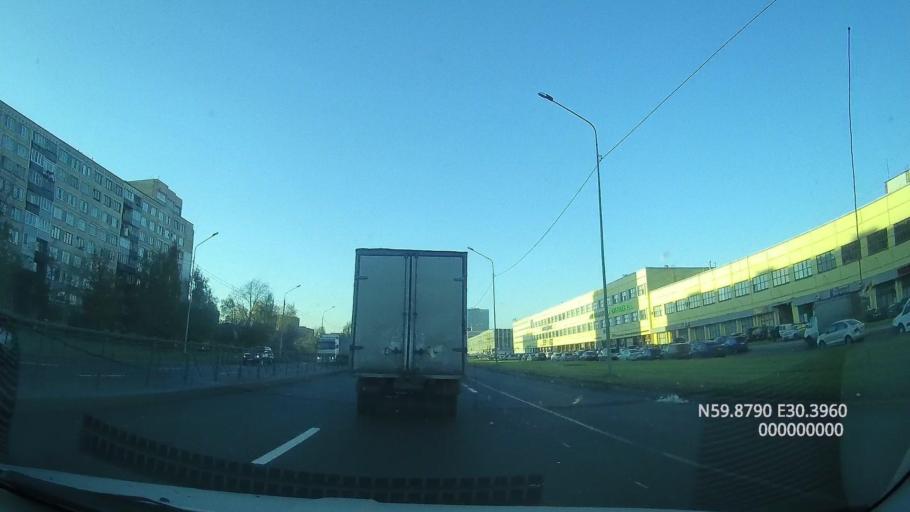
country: RU
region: St.-Petersburg
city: Kupchino
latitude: 59.8791
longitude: 30.3955
